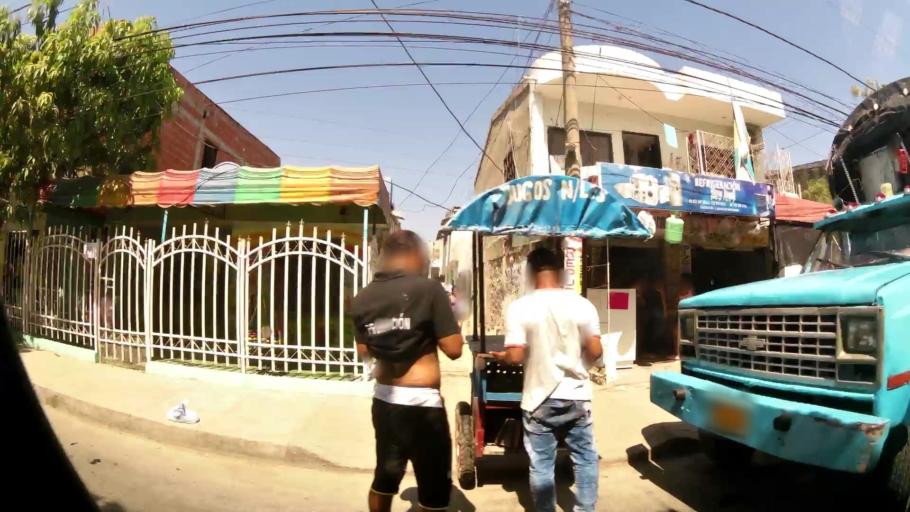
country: CO
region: Bolivar
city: Cartagena
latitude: 10.3851
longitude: -75.4606
